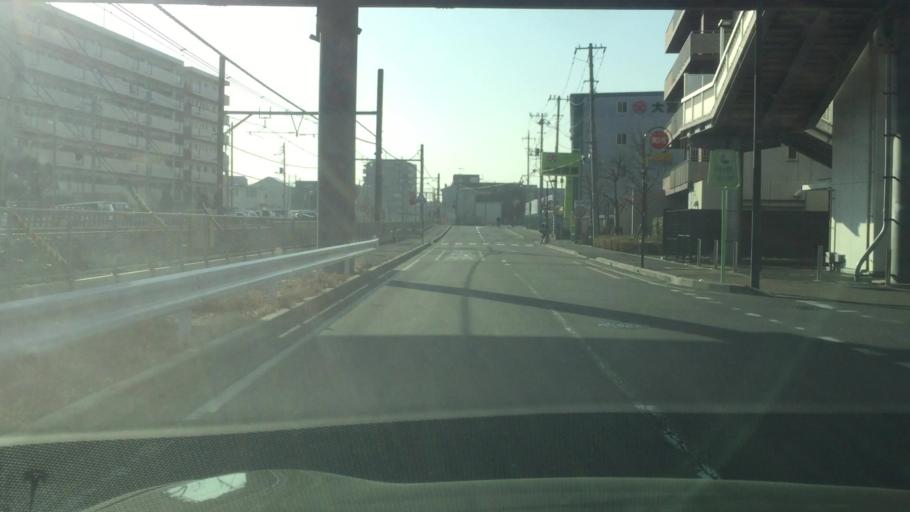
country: JP
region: Saitama
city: Ageoshimo
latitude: 35.9345
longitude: 139.6117
